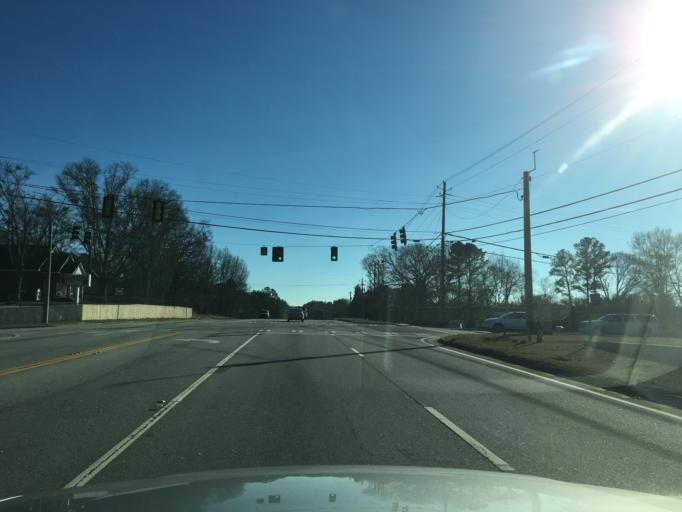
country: US
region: Georgia
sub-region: Carroll County
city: Carrollton
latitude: 33.5418
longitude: -85.0739
